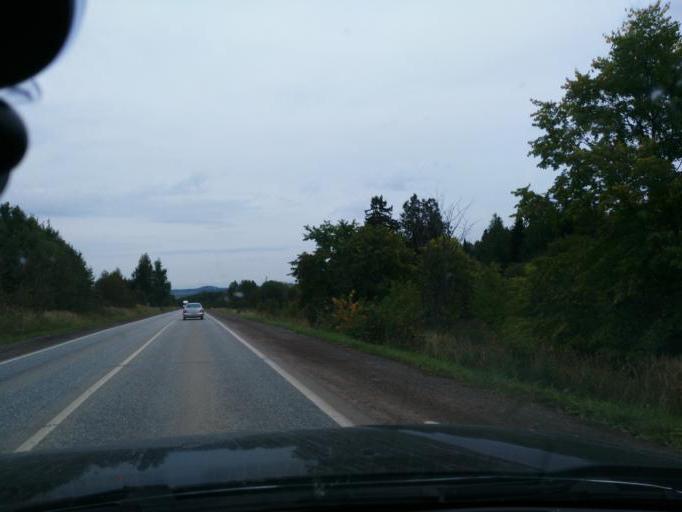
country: RU
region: Perm
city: Chernushka
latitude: 56.5868
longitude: 56.1487
